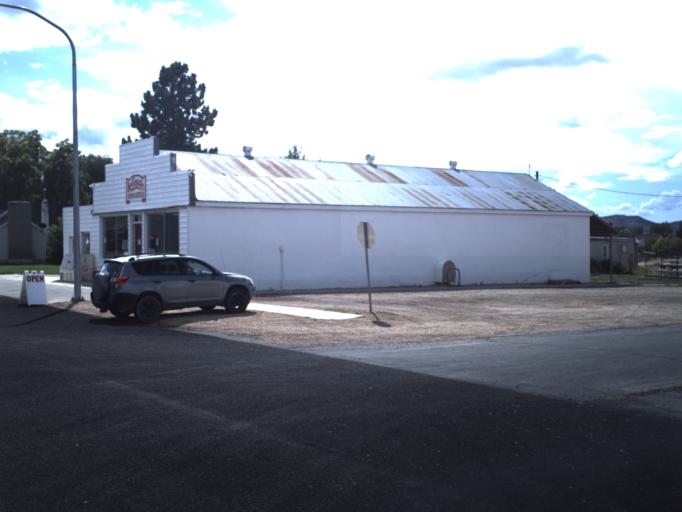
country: US
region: Utah
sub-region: Millard County
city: Fillmore
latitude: 38.8015
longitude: -112.4378
